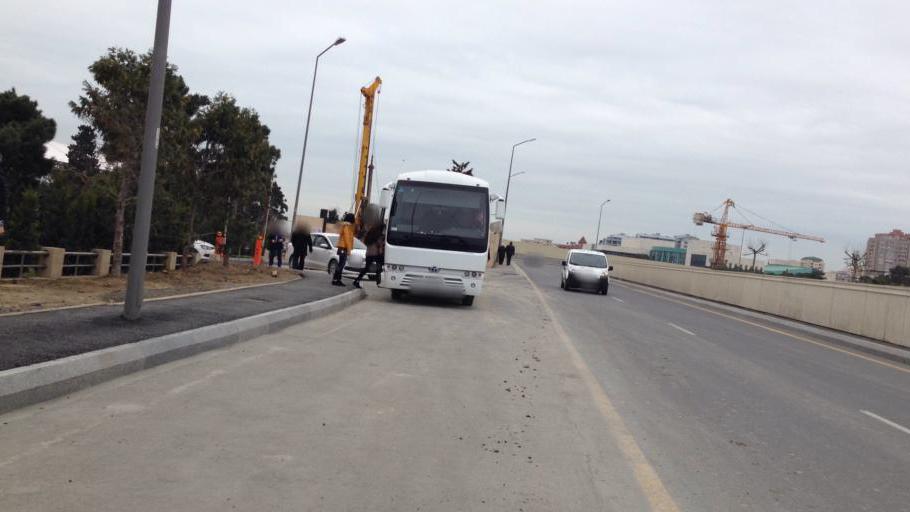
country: AZ
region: Baki
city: Baku
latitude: 40.3989
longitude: 49.8496
